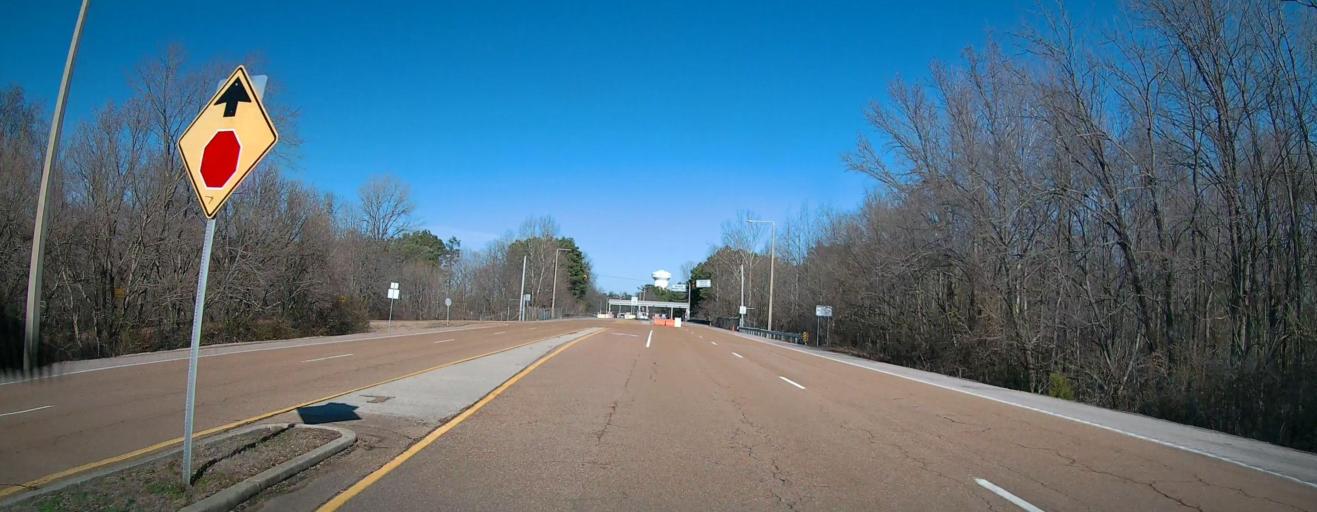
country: US
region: Tennessee
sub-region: Shelby County
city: Millington
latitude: 35.3219
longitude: -89.8711
